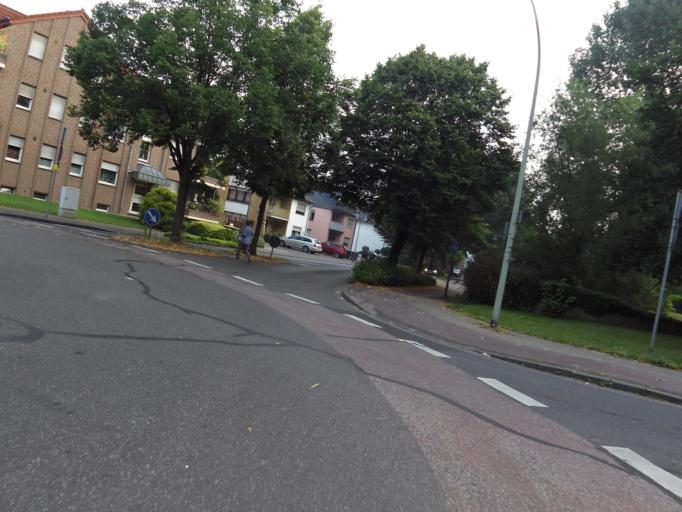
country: DE
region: North Rhine-Westphalia
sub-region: Regierungsbezirk Koln
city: Ubach-Palenberg
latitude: 50.9166
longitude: 6.1160
